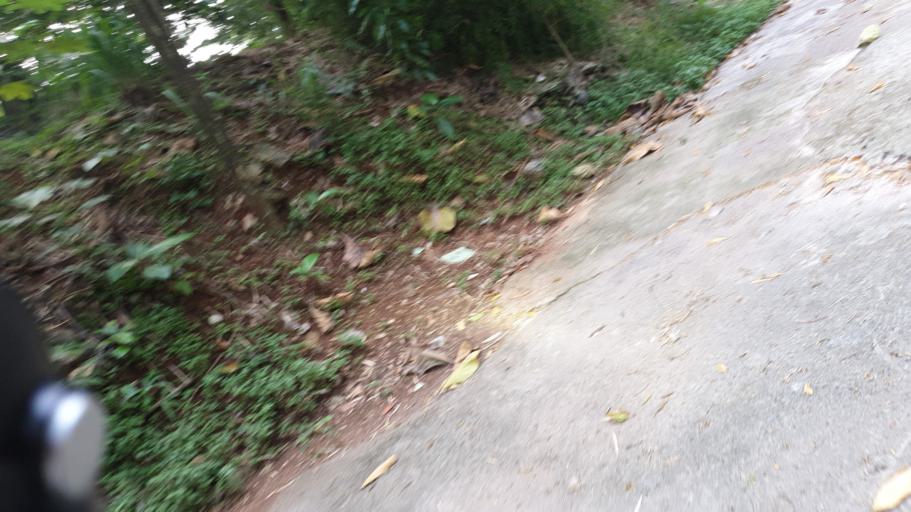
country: ID
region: West Java
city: Depok
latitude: -6.3703
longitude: 106.8386
